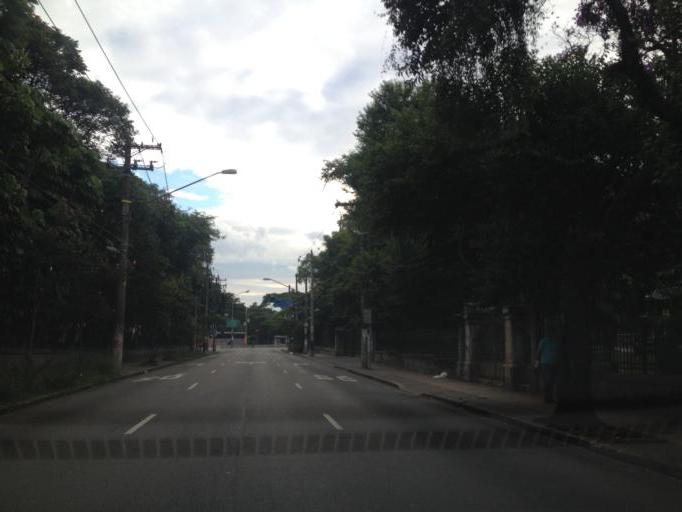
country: BR
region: Sao Paulo
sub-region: Sao Paulo
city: Sao Paulo
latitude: -23.5546
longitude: -46.6726
